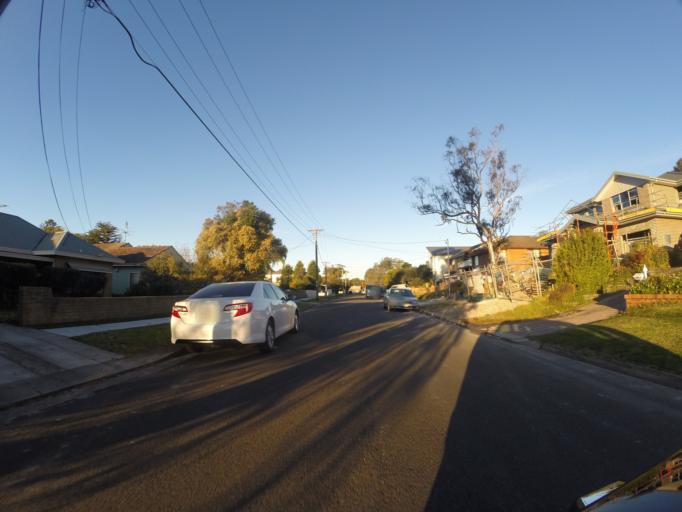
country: AU
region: New South Wales
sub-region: Sutherland Shire
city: Miranda
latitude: -34.0388
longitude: 151.0988
